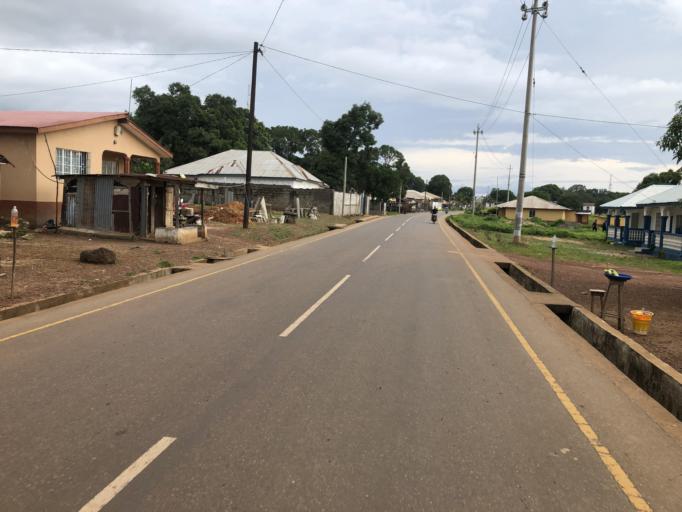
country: SL
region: Northern Province
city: Port Loko
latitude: 8.7705
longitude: -12.7782
